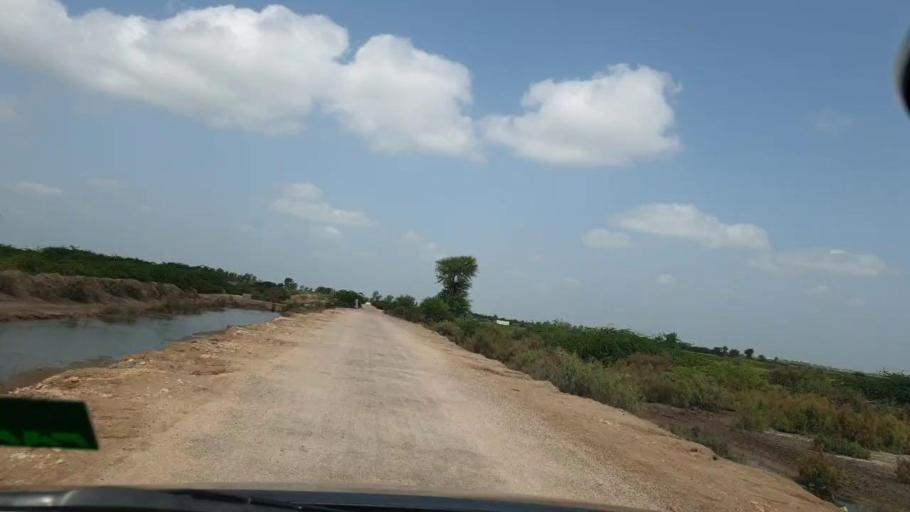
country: PK
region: Sindh
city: Kadhan
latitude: 24.6009
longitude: 69.1236
